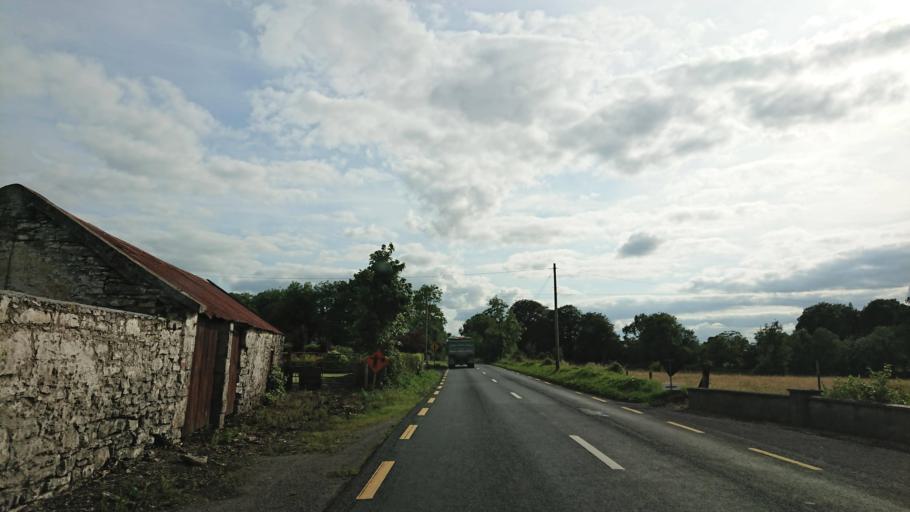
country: IE
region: Connaught
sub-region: County Leitrim
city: Carrick-on-Shannon
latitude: 53.9655
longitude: -8.0718
